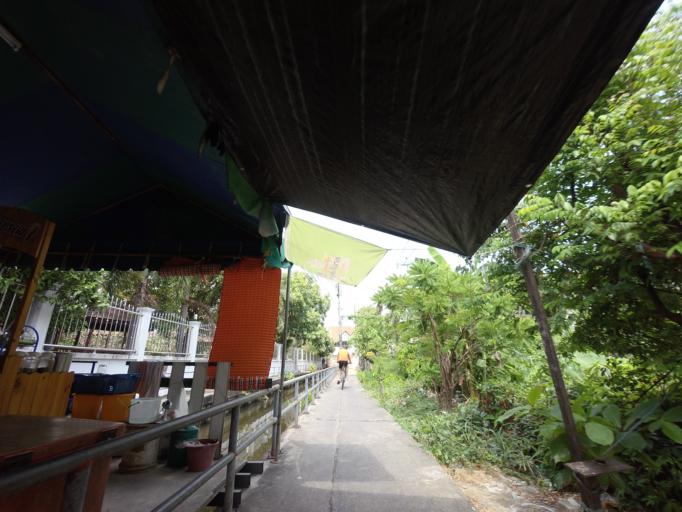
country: TH
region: Bangkok
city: Thung Khru
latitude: 13.6508
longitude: 100.4997
